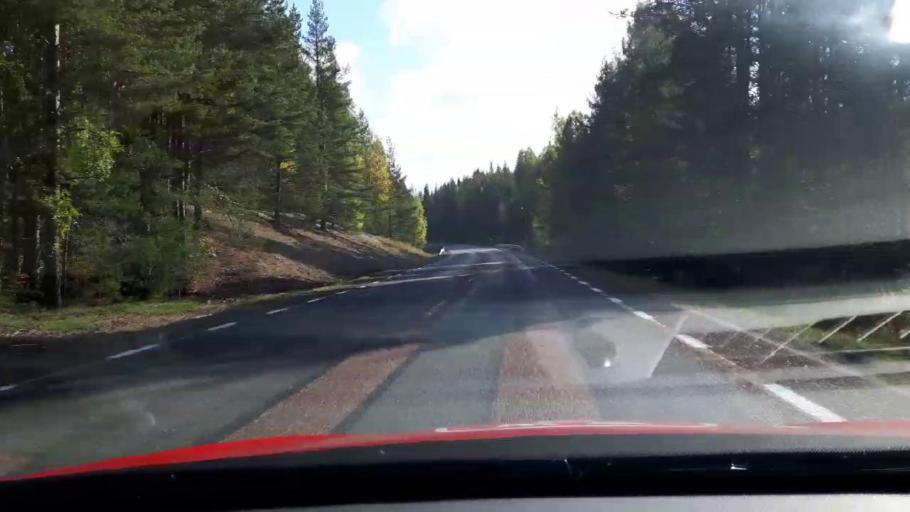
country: SE
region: Gaevleborg
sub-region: Ljusdals Kommun
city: Farila
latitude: 61.8885
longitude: 15.6745
